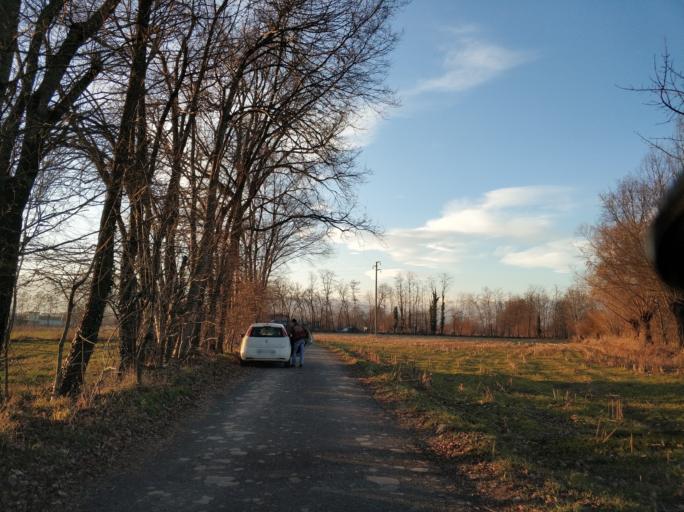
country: IT
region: Piedmont
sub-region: Provincia di Torino
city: Caselle Torinese
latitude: 45.1804
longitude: 7.6322
